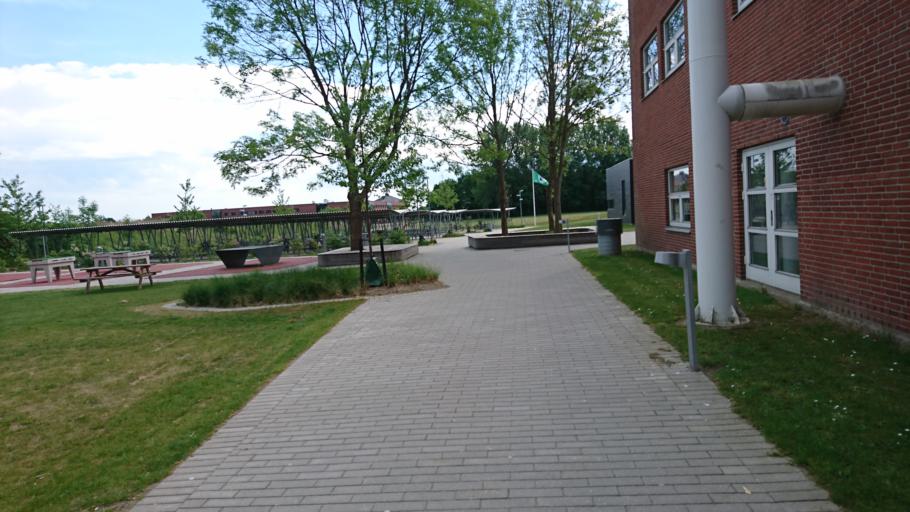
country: DK
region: Capital Region
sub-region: Ballerup Kommune
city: Ballerup
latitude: 55.7360
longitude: 12.3834
